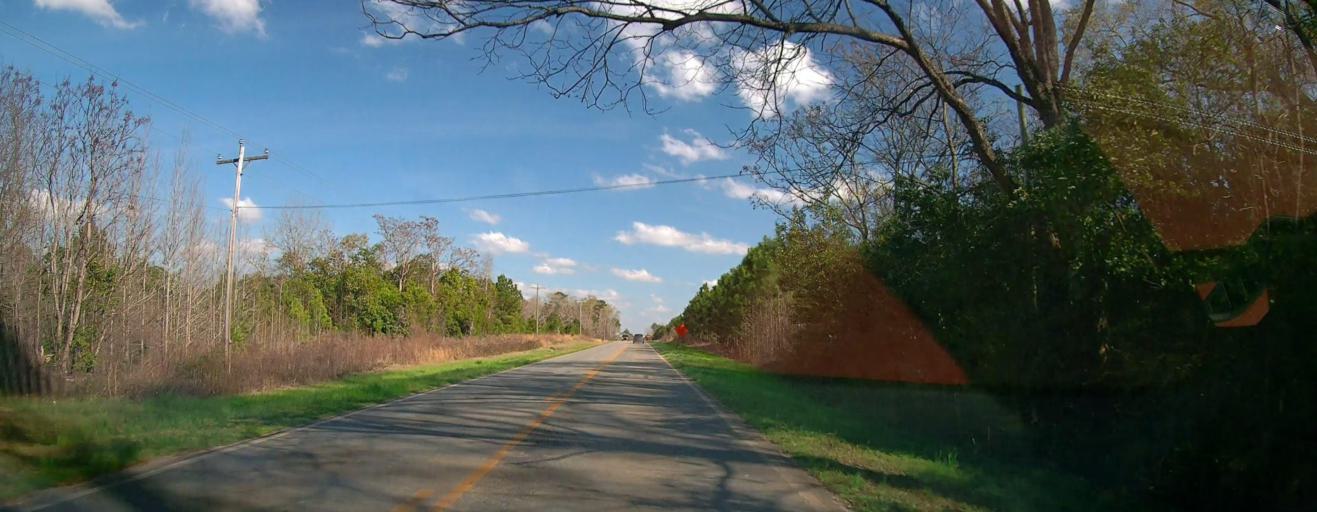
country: US
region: Georgia
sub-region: Laurens County
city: Dublin
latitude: 32.5626
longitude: -83.0160
